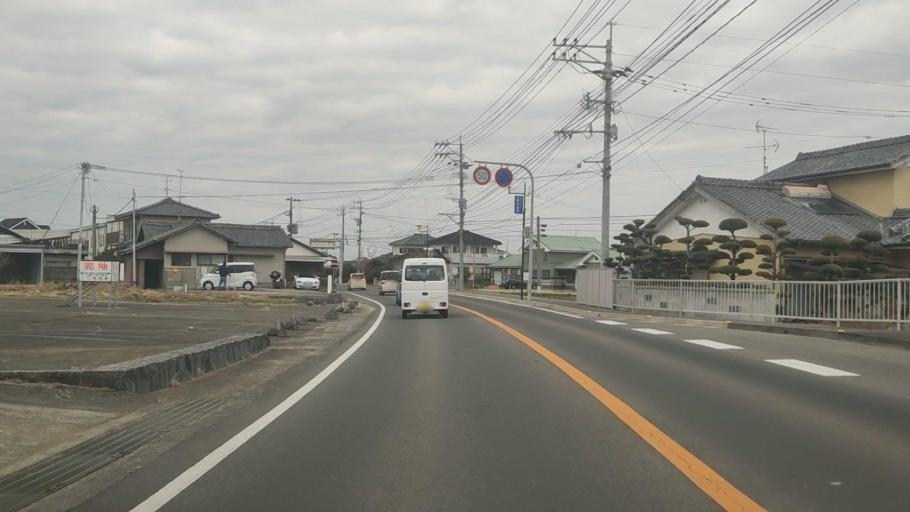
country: JP
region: Nagasaki
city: Shimabara
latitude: 32.8552
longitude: 130.3380
